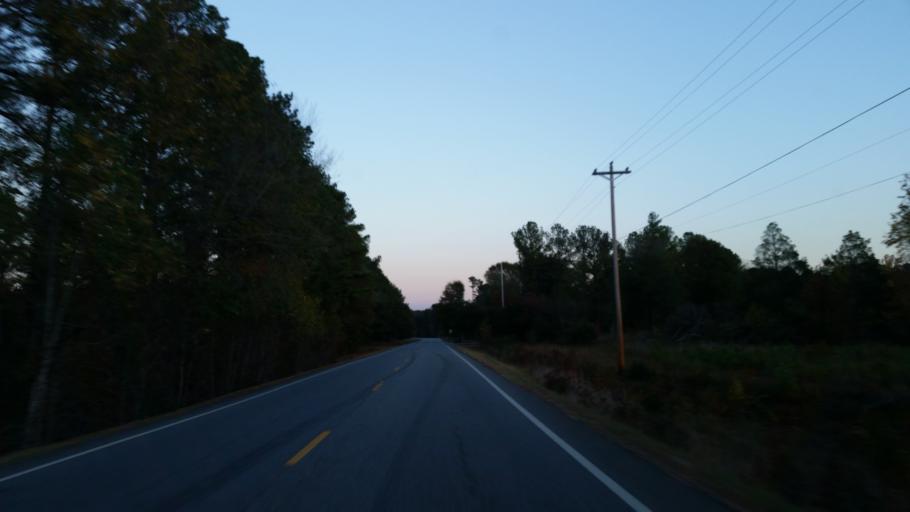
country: US
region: Georgia
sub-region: Gordon County
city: Calhoun
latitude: 34.5762
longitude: -84.9898
